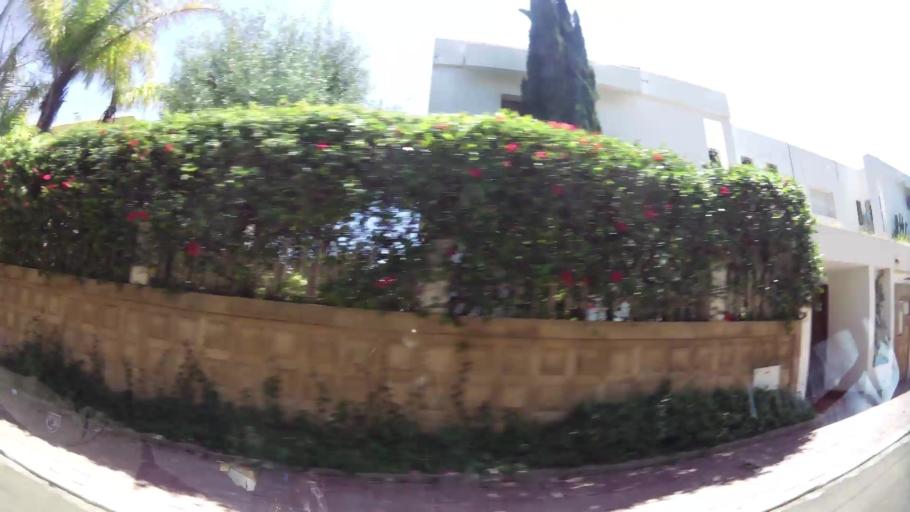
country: MA
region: Souss-Massa-Draa
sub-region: Agadir-Ida-ou-Tnan
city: Agadir
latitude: 30.4294
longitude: -9.5936
